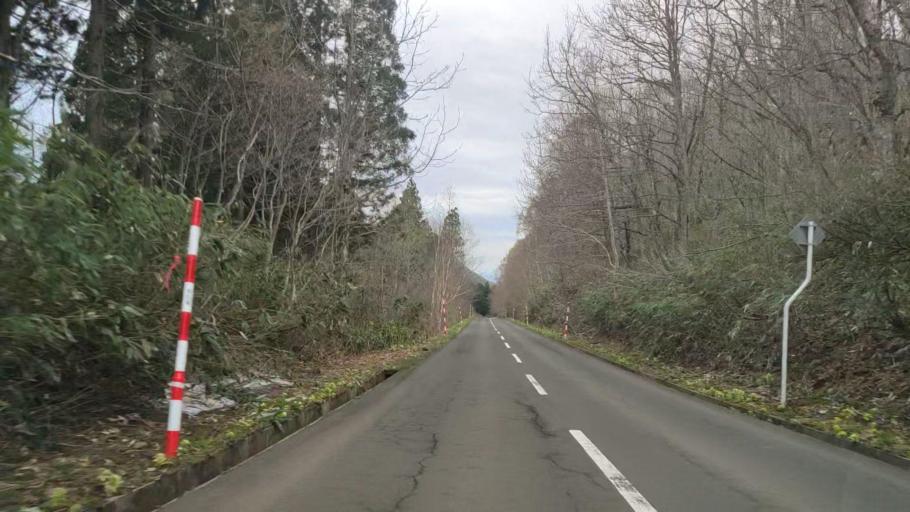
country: JP
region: Akita
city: Hanawa
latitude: 40.4124
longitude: 140.8180
